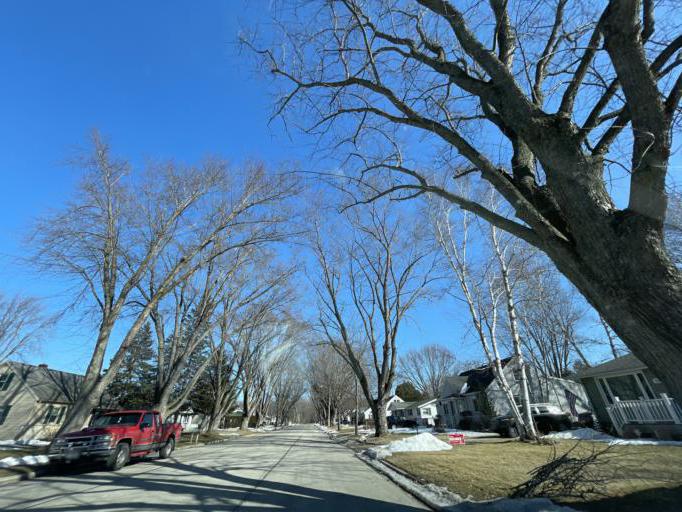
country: US
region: Wisconsin
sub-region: Brown County
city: Howard
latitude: 44.5675
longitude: -88.0843
